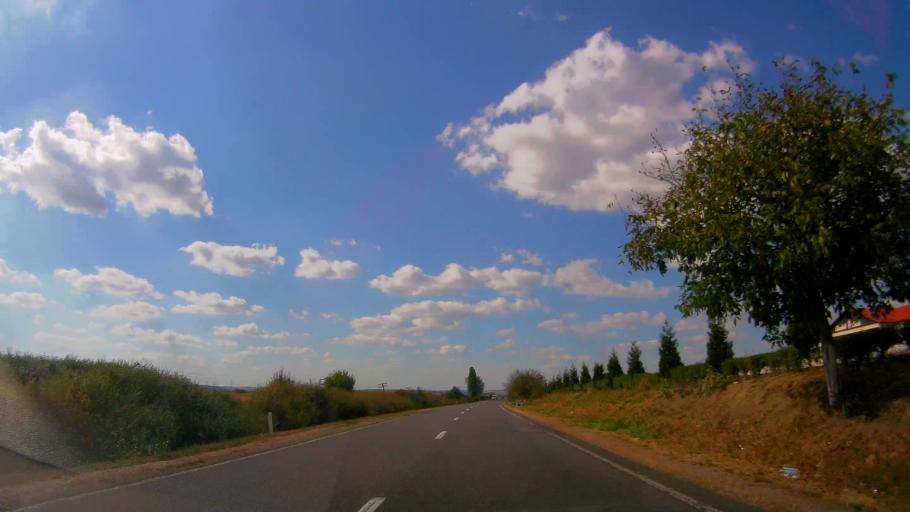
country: RO
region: Salaj
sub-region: Comuna Sarmasag
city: Sarmasag
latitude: 47.3305
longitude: 22.8600
